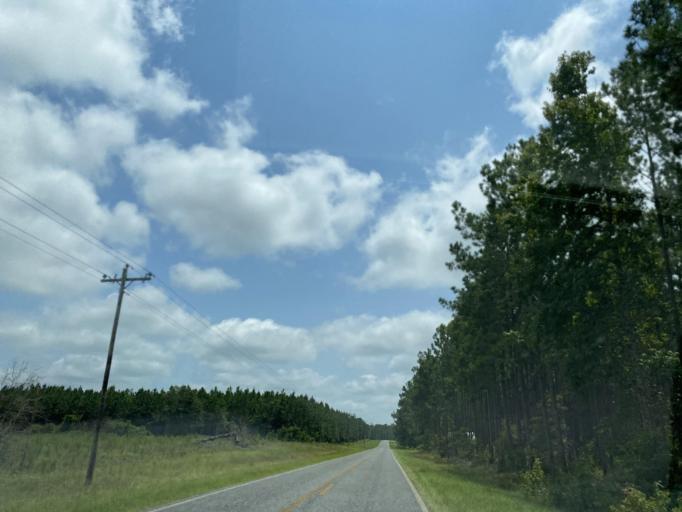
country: US
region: Georgia
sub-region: Wheeler County
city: Alamo
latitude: 32.1110
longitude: -82.7799
